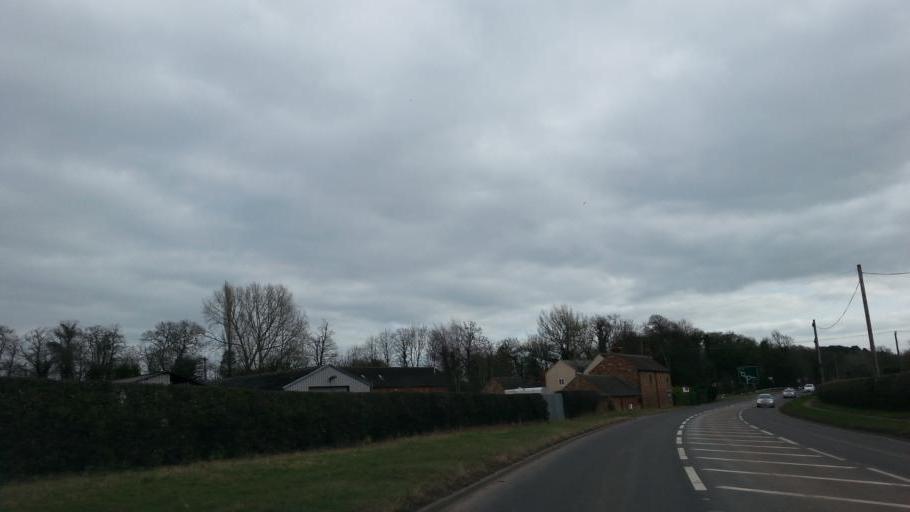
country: GB
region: England
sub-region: Staffordshire
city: Colwich
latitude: 52.7838
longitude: -1.9732
